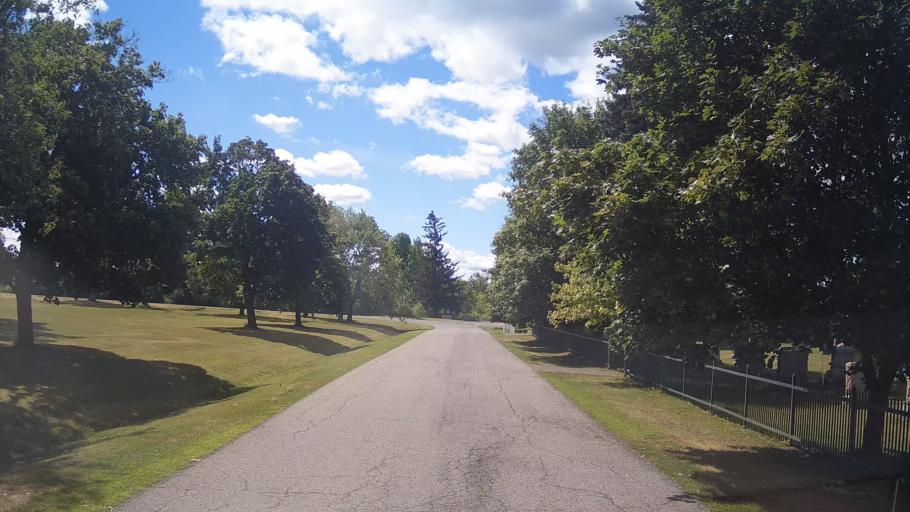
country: US
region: New York
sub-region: St. Lawrence County
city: Ogdensburg
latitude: 44.8307
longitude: -75.3152
